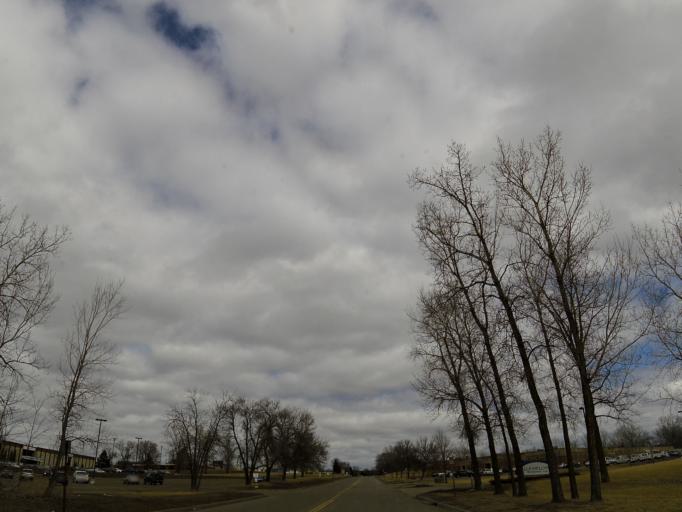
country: US
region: Minnesota
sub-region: Washington County
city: Woodbury
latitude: 44.9173
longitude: -92.9748
